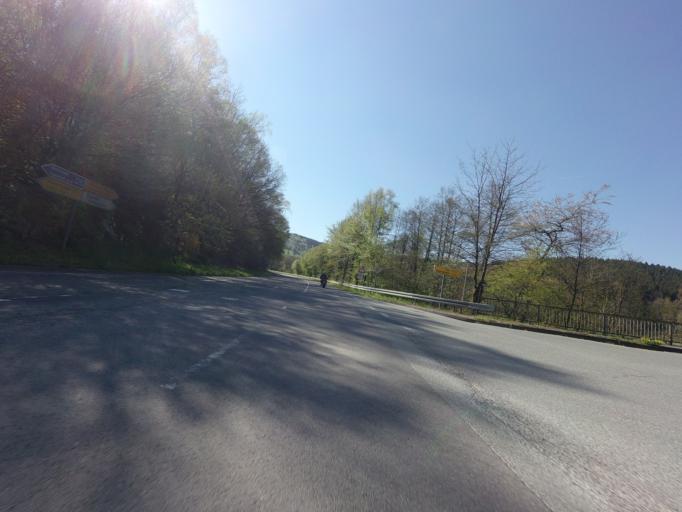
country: DE
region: North Rhine-Westphalia
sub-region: Regierungsbezirk Arnsberg
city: Drolshagen
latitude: 51.0797
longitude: 7.7584
